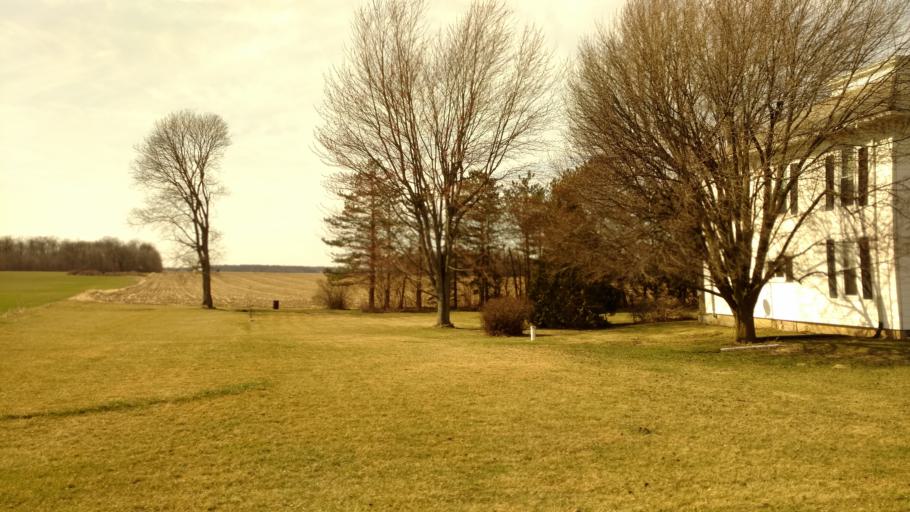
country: US
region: Ohio
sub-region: Hardin County
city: Kenton
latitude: 40.5879
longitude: -83.5050
